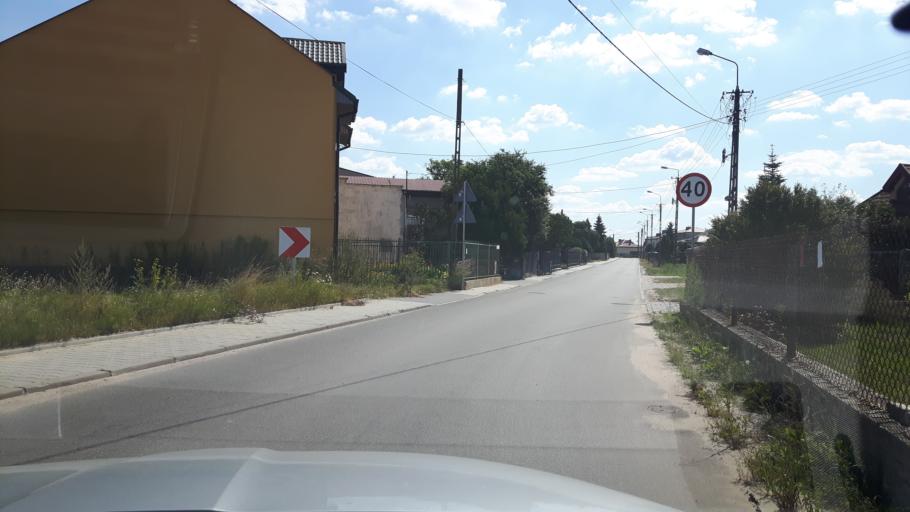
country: PL
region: Masovian Voivodeship
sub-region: Powiat pruszkowski
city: Nowe Grocholice
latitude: 52.1143
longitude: 20.8737
